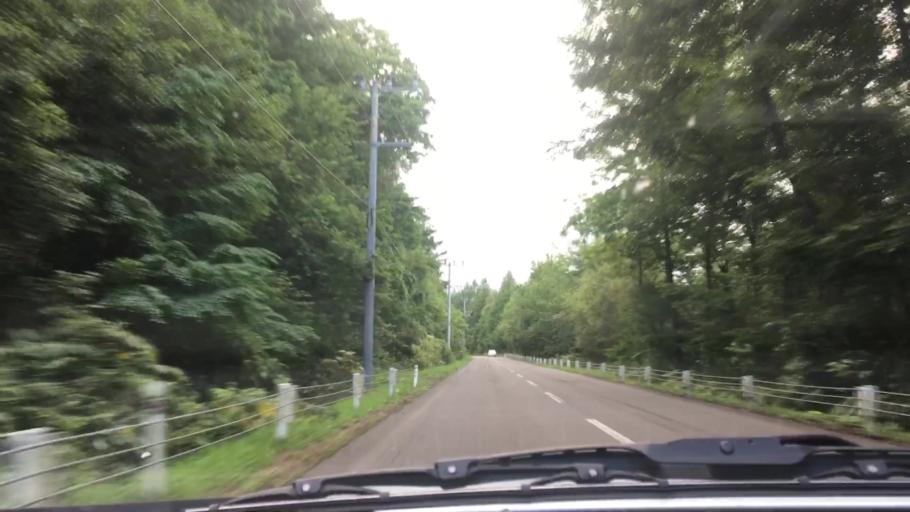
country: JP
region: Hokkaido
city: Otofuke
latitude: 43.1462
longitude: 142.8740
